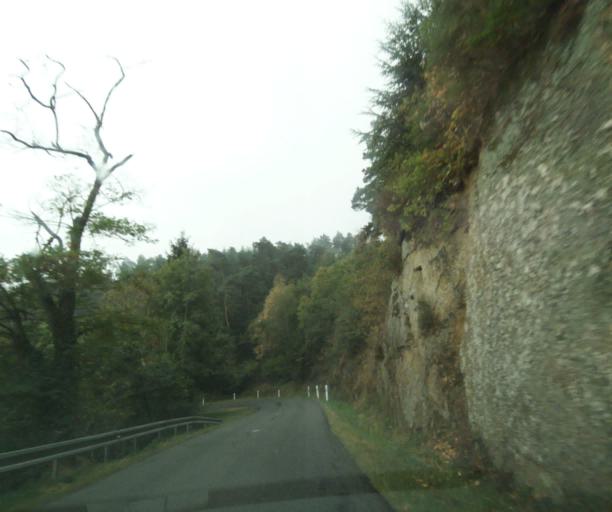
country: FR
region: Auvergne
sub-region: Departement du Puy-de-Dome
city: Ceyrat
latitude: 45.7307
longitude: 3.0574
